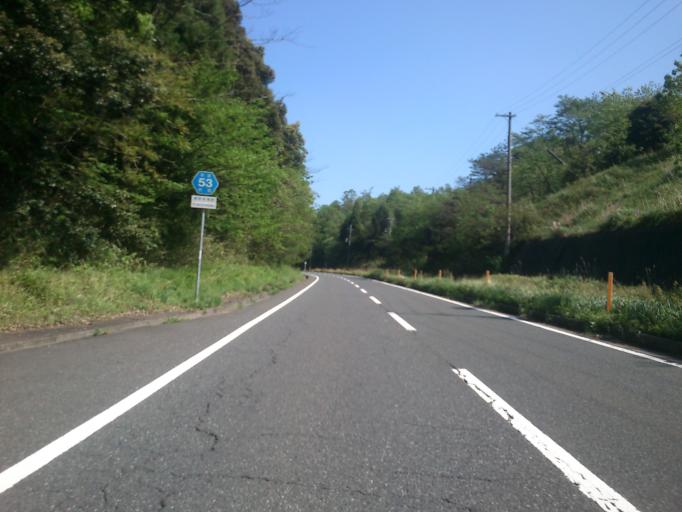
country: JP
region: Kyoto
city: Miyazu
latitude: 35.6612
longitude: 135.1035
